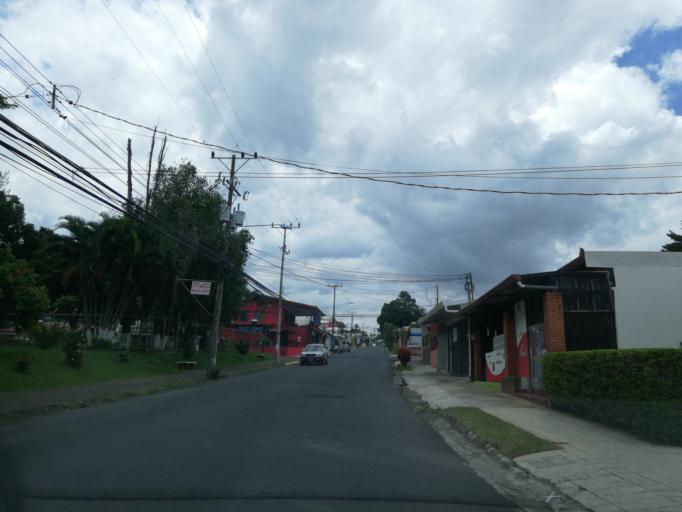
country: CR
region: Alajuela
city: Alajuela
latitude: 10.0124
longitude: -84.2281
